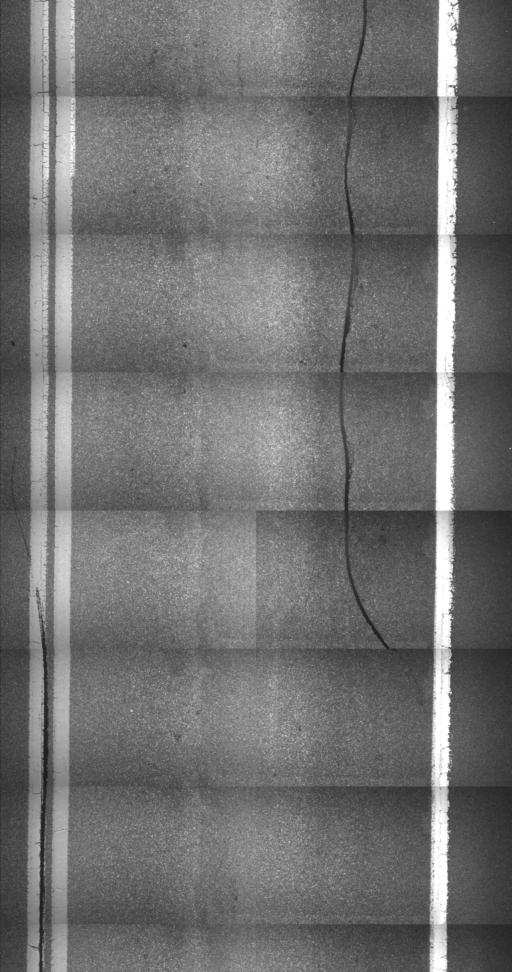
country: US
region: Vermont
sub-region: Bennington County
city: Manchester Center
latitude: 43.2991
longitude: -73.1458
